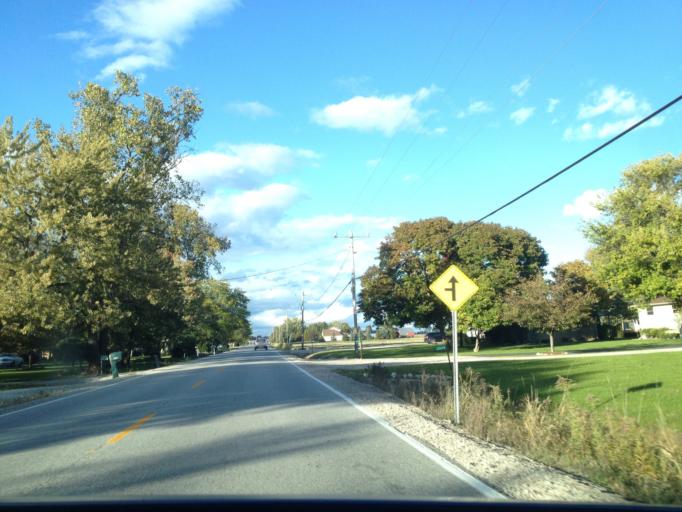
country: US
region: Michigan
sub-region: Wayne County
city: Grosse Pointe
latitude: 42.2282
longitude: -82.7140
